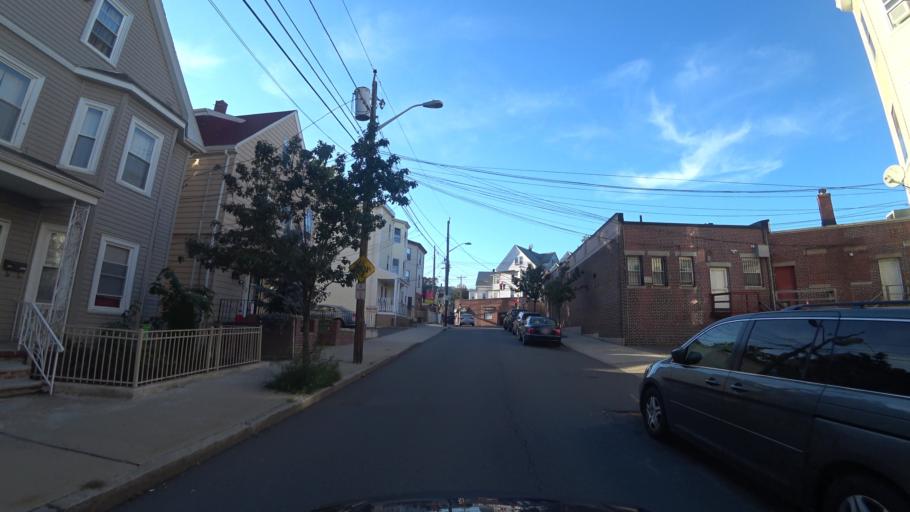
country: US
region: Massachusetts
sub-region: Middlesex County
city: Everett
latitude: 42.4132
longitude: -71.0383
